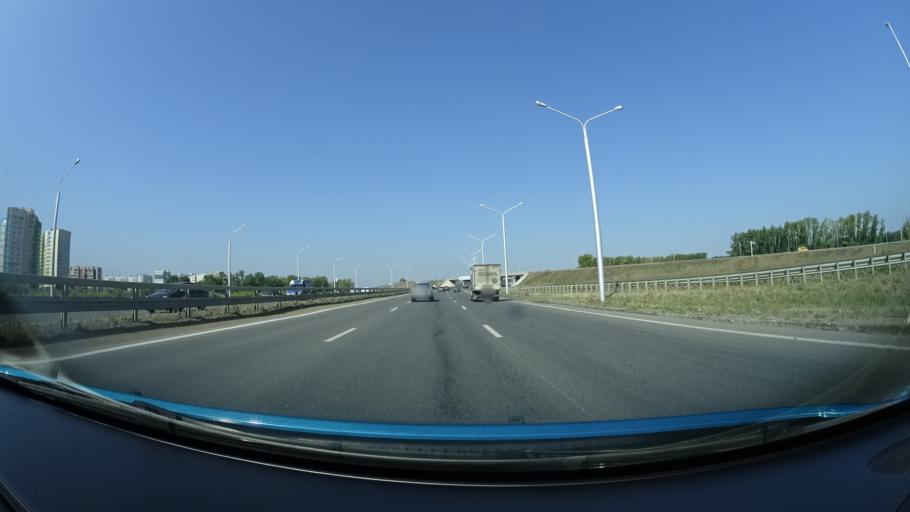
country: RU
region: Bashkortostan
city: Mikhaylovka
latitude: 54.7983
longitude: 55.8705
